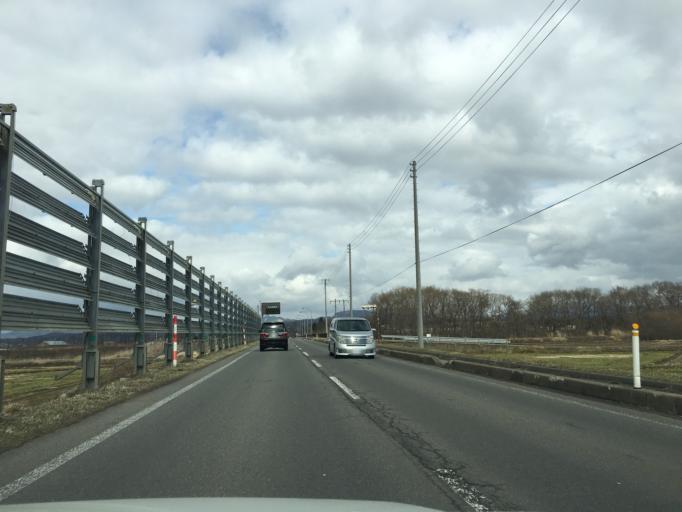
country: JP
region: Akita
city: Hanawa
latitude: 40.2520
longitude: 140.7588
